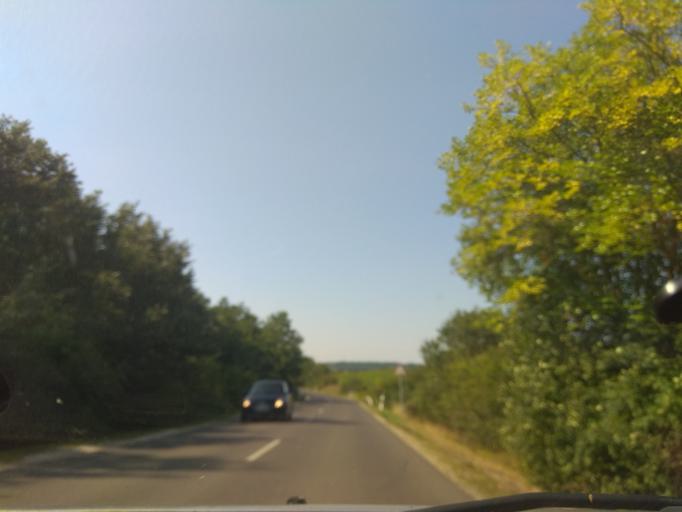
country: HU
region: Borsod-Abauj-Zemplen
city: Harsany
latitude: 47.9864
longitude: 20.7493
